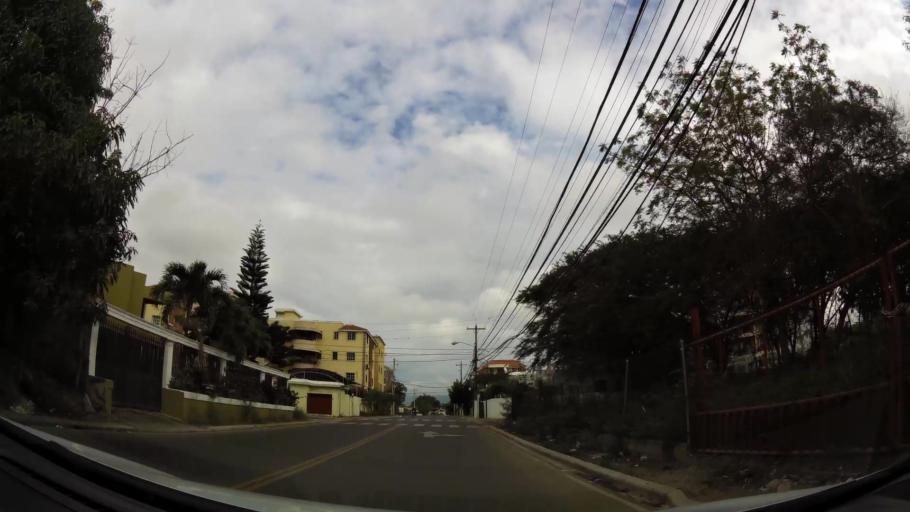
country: DO
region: Santiago
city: Santiago de los Caballeros
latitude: 19.4643
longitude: -70.6575
